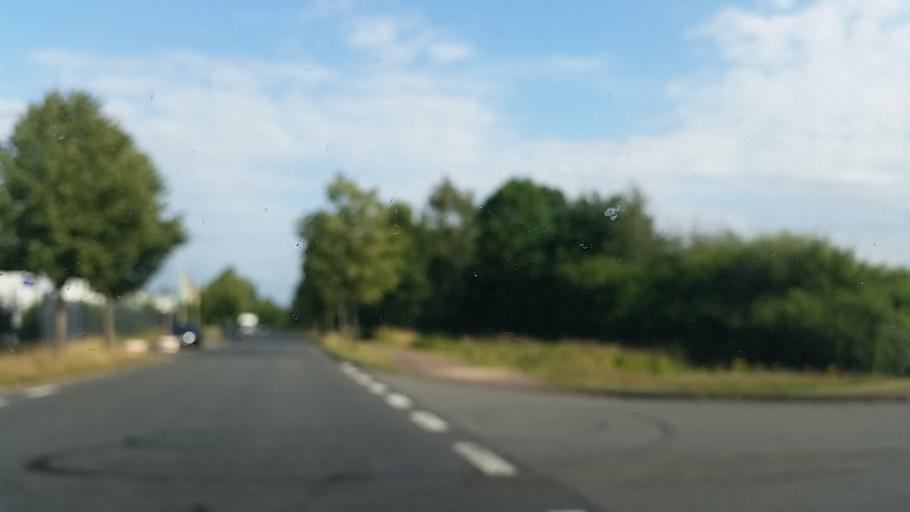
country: DE
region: Lower Saxony
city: Winsen
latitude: 53.3389
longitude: 10.2314
